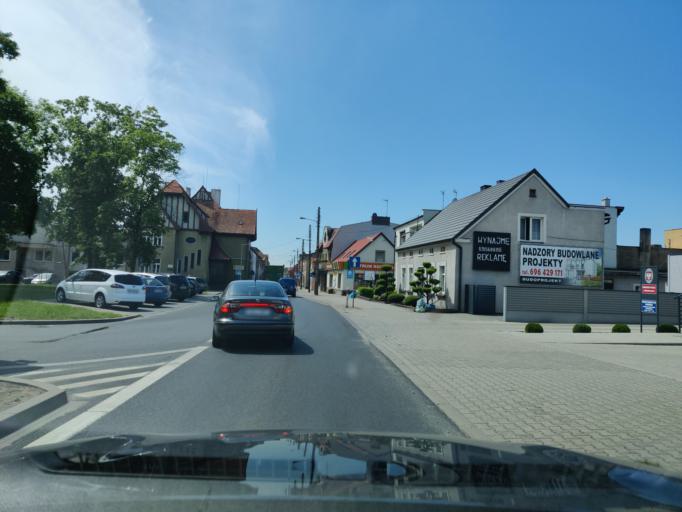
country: PL
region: Greater Poland Voivodeship
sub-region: Powiat grodziski
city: Rakoniewice
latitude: 52.1416
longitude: 16.2758
